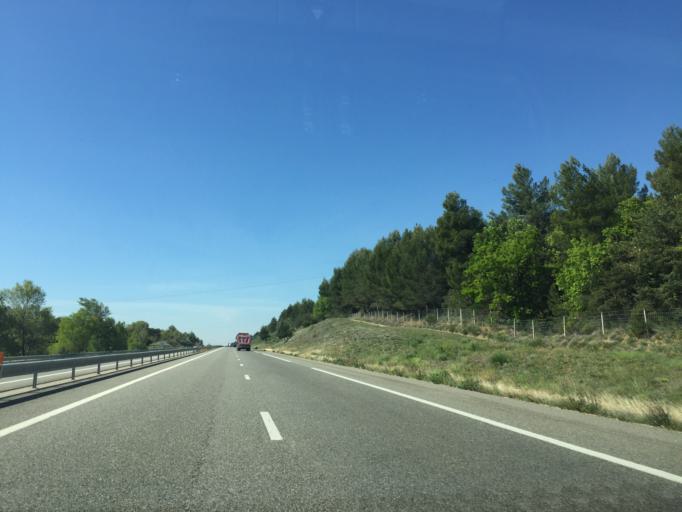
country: FR
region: Provence-Alpes-Cote d'Azur
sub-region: Departement des Alpes-de-Haute-Provence
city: Volonne
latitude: 44.0847
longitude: 5.9853
